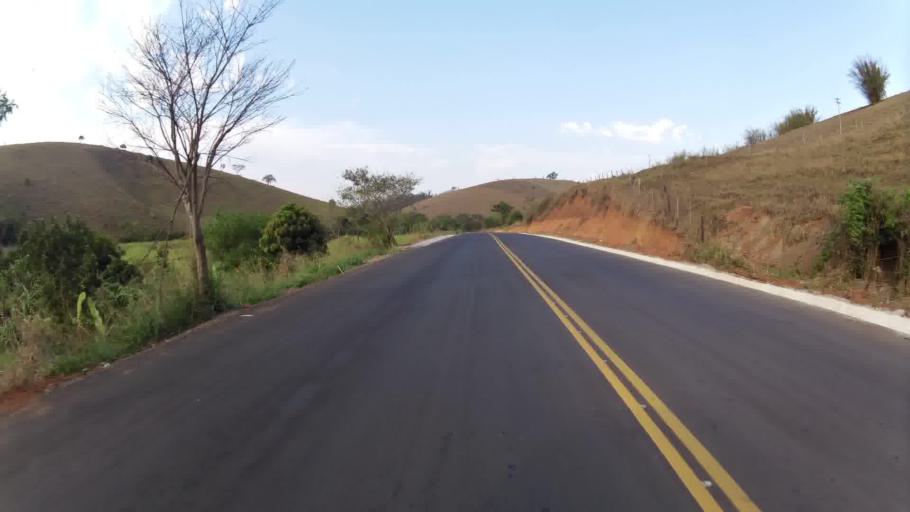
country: BR
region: Rio de Janeiro
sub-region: Santo Antonio De Padua
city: Santo Antonio de Padua
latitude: -21.4878
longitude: -42.0627
